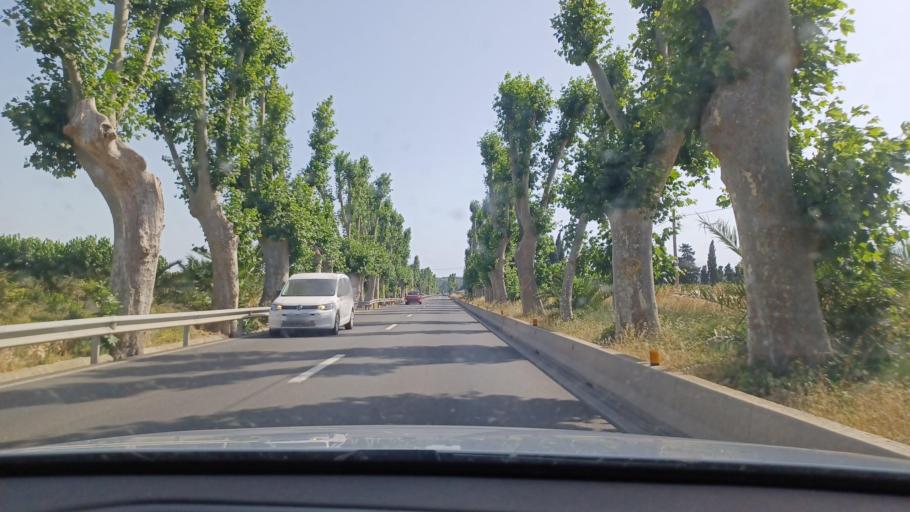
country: ES
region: Catalonia
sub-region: Provincia de Tarragona
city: Tortosa
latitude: 40.8017
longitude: 0.5022
